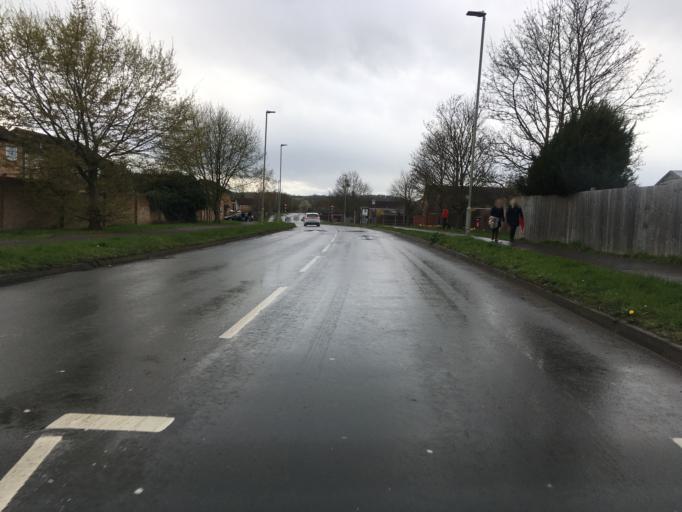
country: GB
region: England
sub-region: Gloucestershire
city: Gloucester
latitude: 51.8187
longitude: -2.2823
